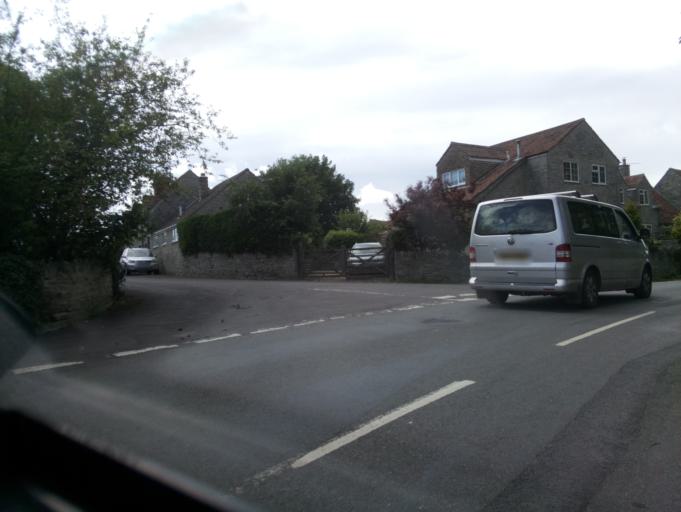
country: GB
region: England
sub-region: Somerset
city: Ilchester
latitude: 51.0585
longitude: -2.6735
